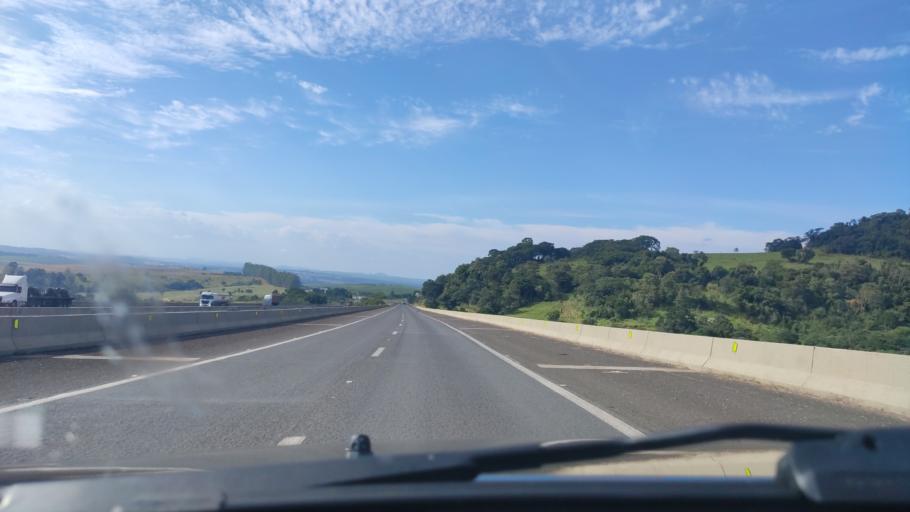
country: BR
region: Sao Paulo
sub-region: Itatinga
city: Itatinga
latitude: -23.1045
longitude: -48.5059
